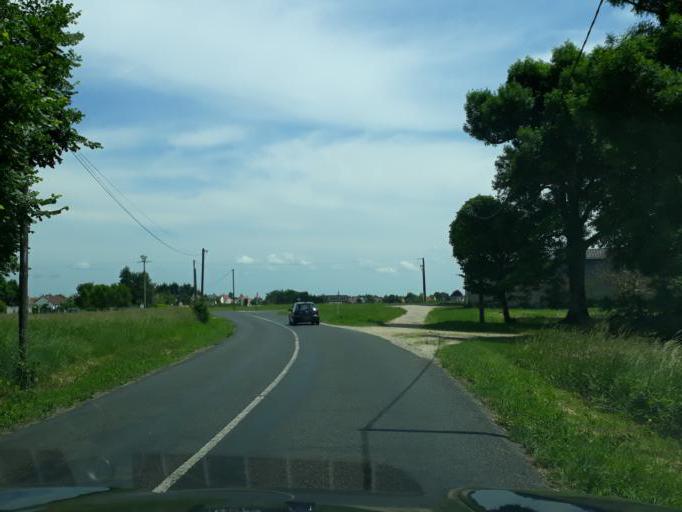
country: FR
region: Centre
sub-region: Departement du Loiret
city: Sandillon
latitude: 47.8411
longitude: 2.0121
